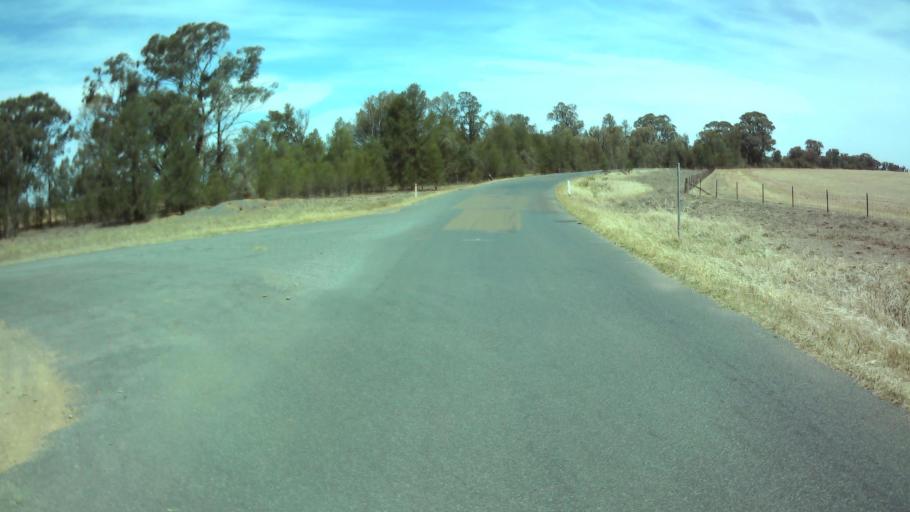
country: AU
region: New South Wales
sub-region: Weddin
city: Grenfell
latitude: -33.9442
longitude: 147.7785
